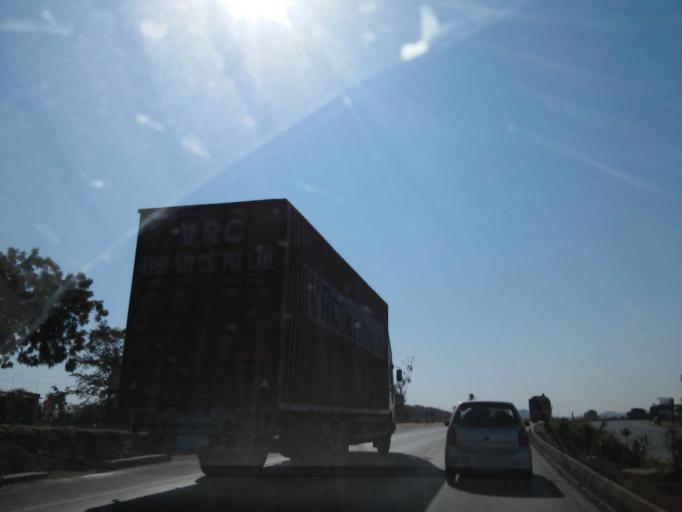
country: IN
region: Rajasthan
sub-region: Dungarpur
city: Dungarpur
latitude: 24.0148
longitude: 73.6574
